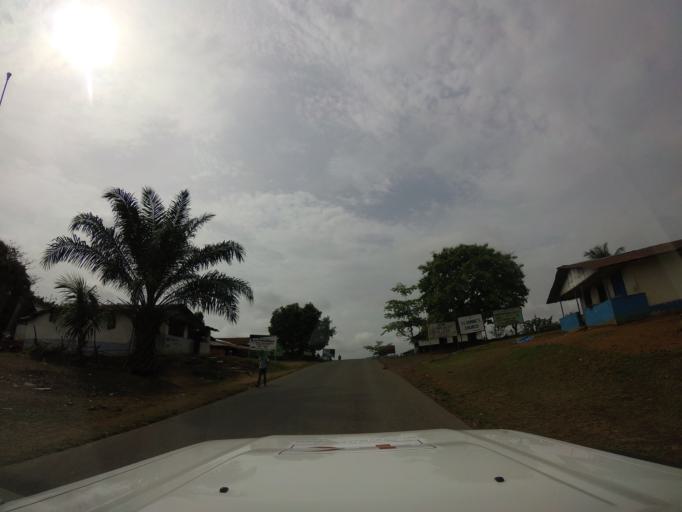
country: LR
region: Bomi
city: Tubmanburg
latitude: 6.8650
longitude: -10.8186
